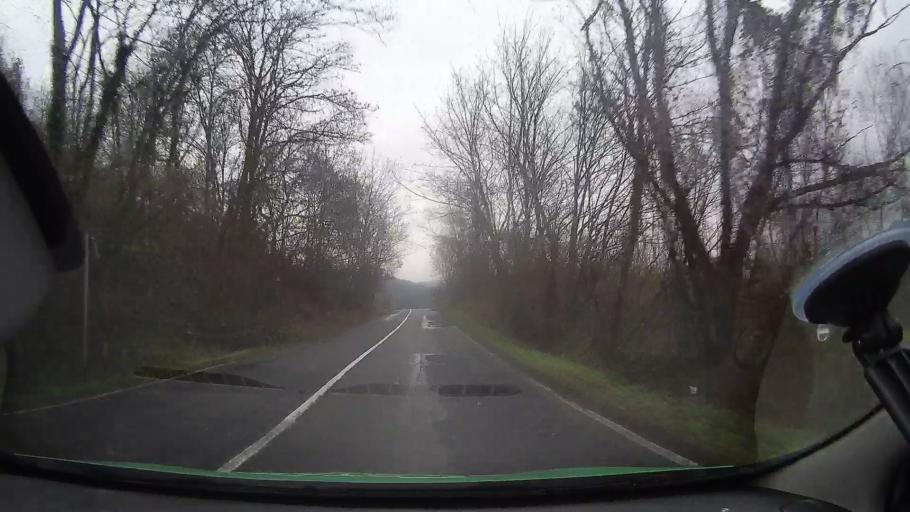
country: RO
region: Arad
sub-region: Comuna Gurahont
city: Gurahont
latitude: 46.2816
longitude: 22.3758
